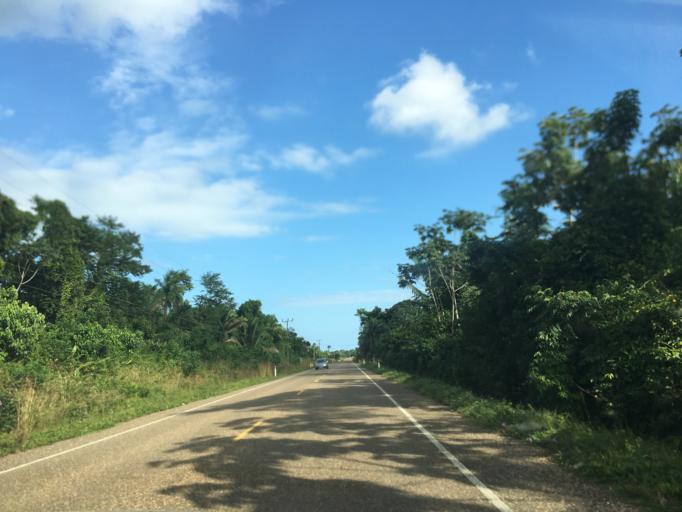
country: BZ
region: Stann Creek
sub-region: Dangriga
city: Dangriga
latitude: 16.8546
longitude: -88.3244
